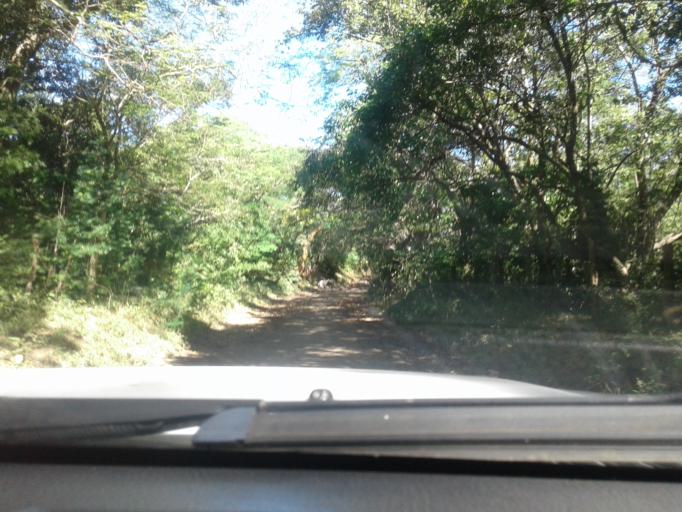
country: NI
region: Carazo
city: Santa Teresa
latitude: 11.7791
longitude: -86.1798
